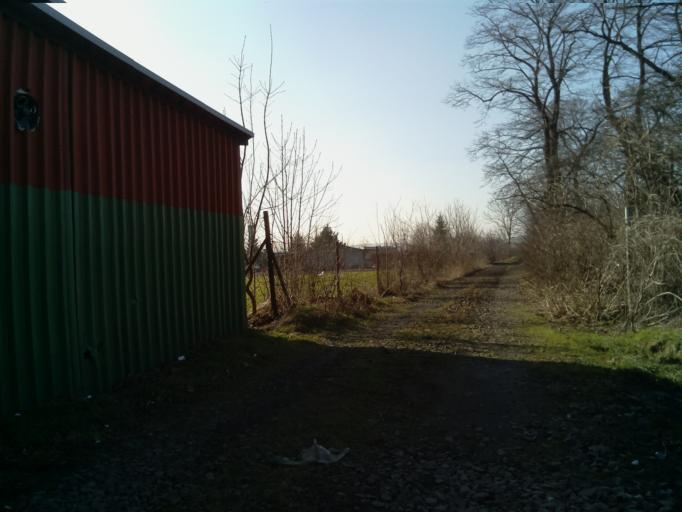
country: PL
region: Lower Silesian Voivodeship
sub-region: Powiat swidnicki
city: Swiebodzice
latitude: 50.8713
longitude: 16.3500
